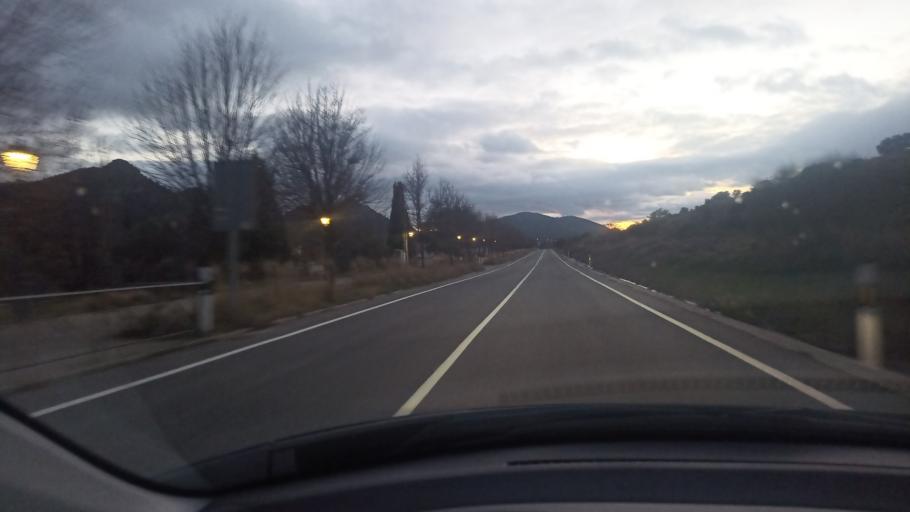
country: ES
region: Madrid
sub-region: Provincia de Madrid
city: Robledo de Chavela
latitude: 40.4954
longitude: -4.2416
